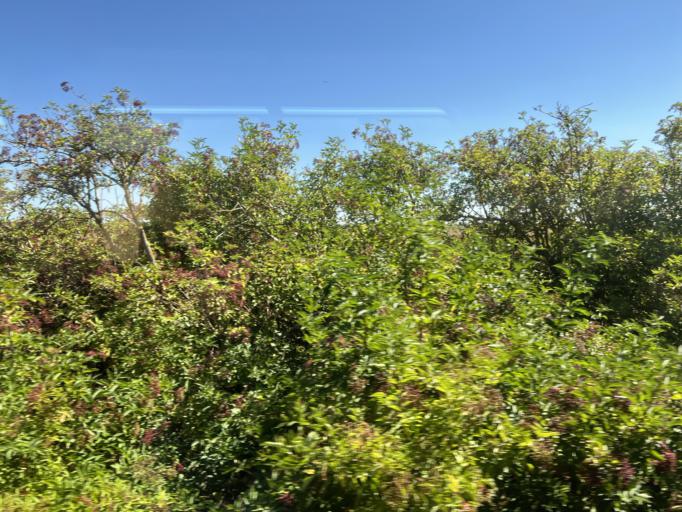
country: GB
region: England
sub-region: Lincolnshire
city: Spilsby
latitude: 53.1266
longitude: 0.1446
